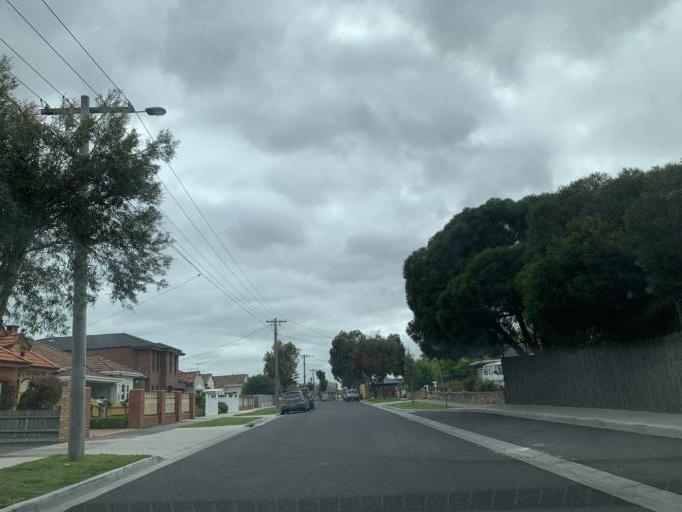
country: AU
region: Victoria
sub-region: Moreland
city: Pascoe Vale South
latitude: -37.7404
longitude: 144.9423
